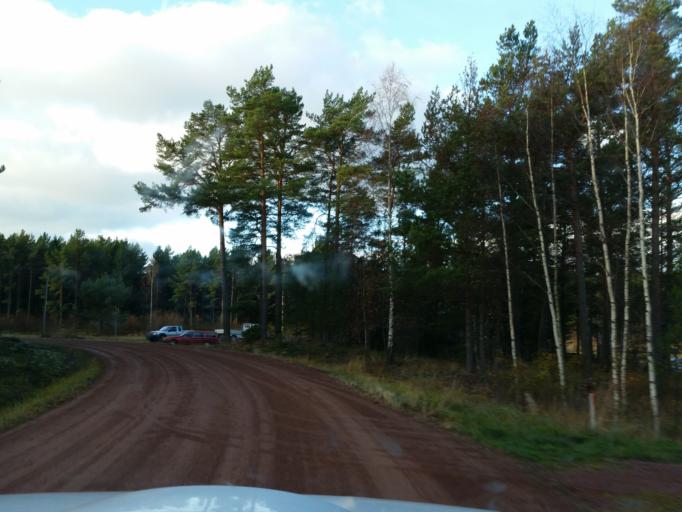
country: AX
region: Alands skaergard
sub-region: Foegloe
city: Foegloe
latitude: 59.9966
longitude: 20.3359
